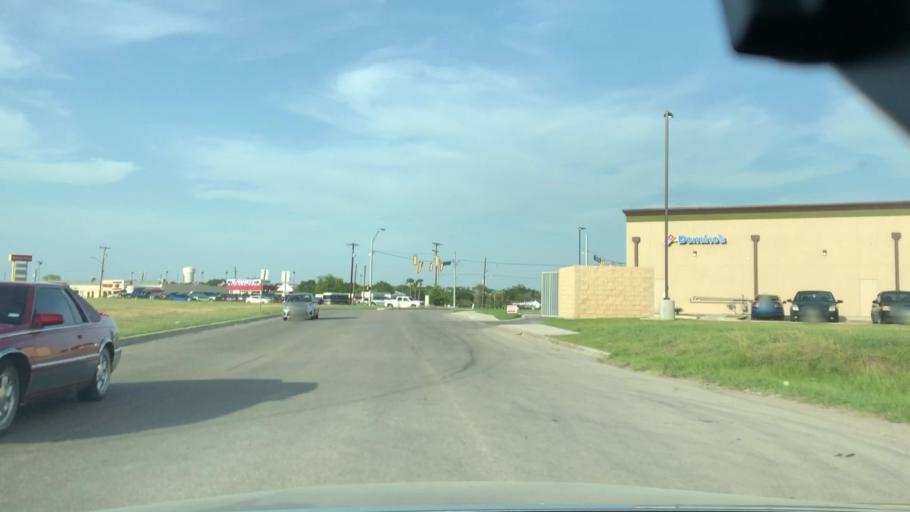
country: US
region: Texas
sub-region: Bexar County
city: Converse
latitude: 29.5133
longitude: -98.3095
